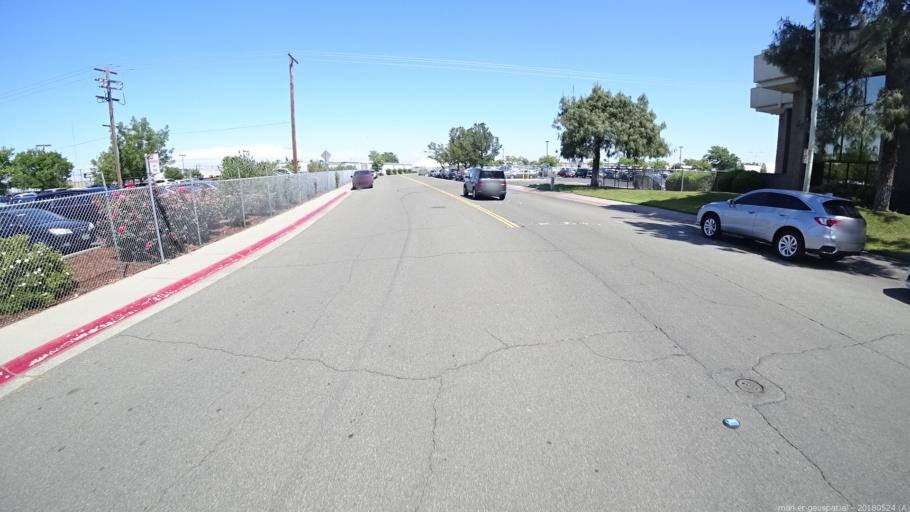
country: US
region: California
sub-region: Sacramento County
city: Sacramento
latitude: 38.6048
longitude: -121.4476
